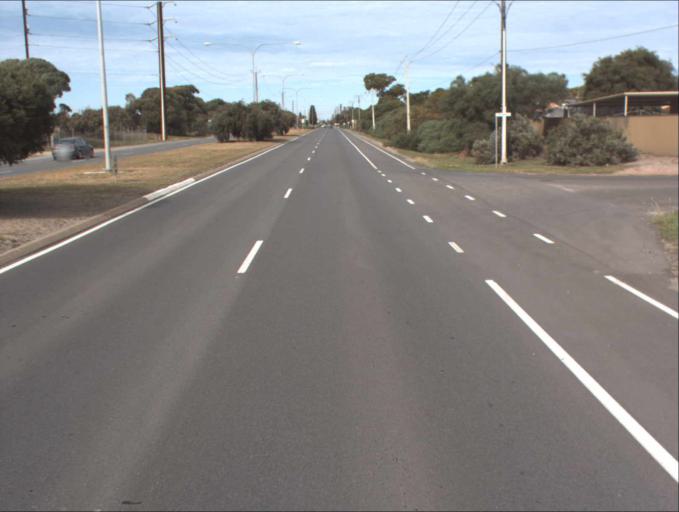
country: AU
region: South Australia
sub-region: Port Adelaide Enfield
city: Birkenhead
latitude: -34.7867
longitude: 138.5014
